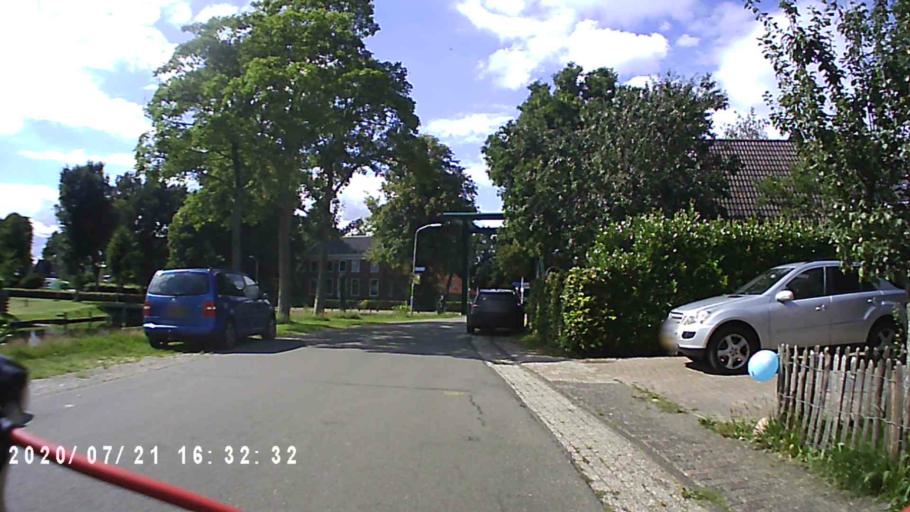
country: NL
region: Groningen
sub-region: Gemeente Hoogezand-Sappemeer
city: Sappemeer
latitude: 53.0848
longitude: 6.7908
